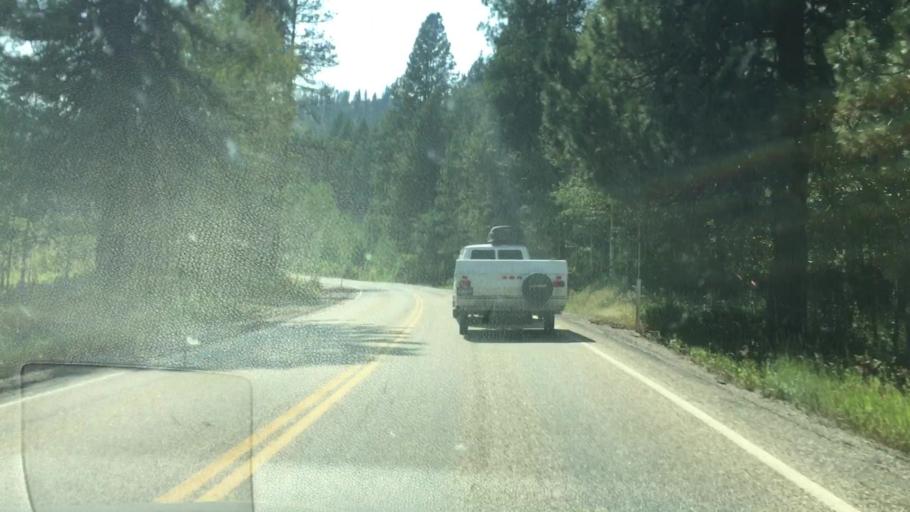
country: US
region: Idaho
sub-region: Valley County
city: Cascade
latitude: 44.3128
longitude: -116.0816
